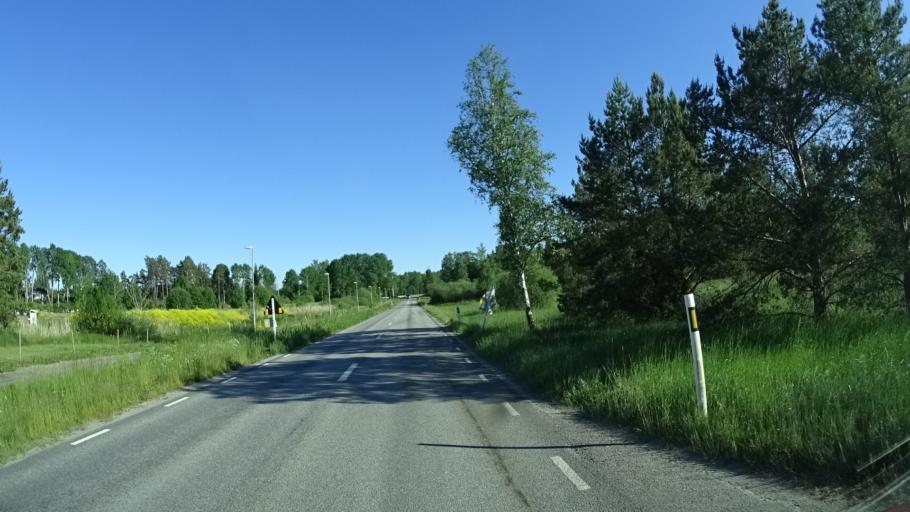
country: SE
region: Stockholm
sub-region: Vallentuna Kommun
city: Vallentuna
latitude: 59.5664
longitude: 18.1015
